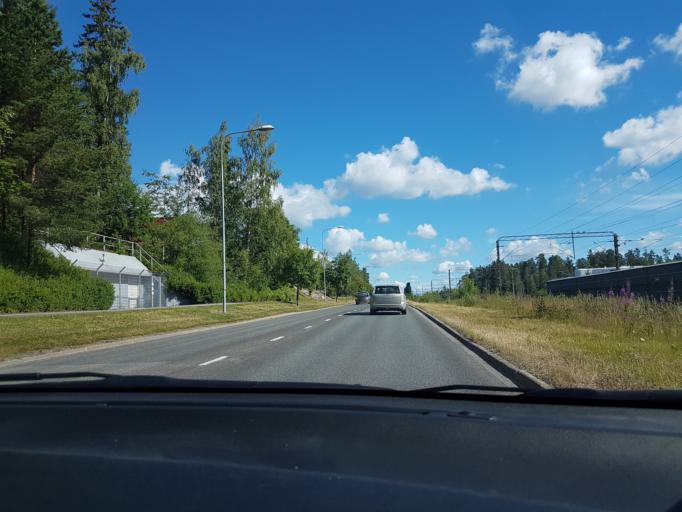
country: FI
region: Uusimaa
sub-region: Helsinki
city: Kerava
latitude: 60.3763
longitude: 25.0957
